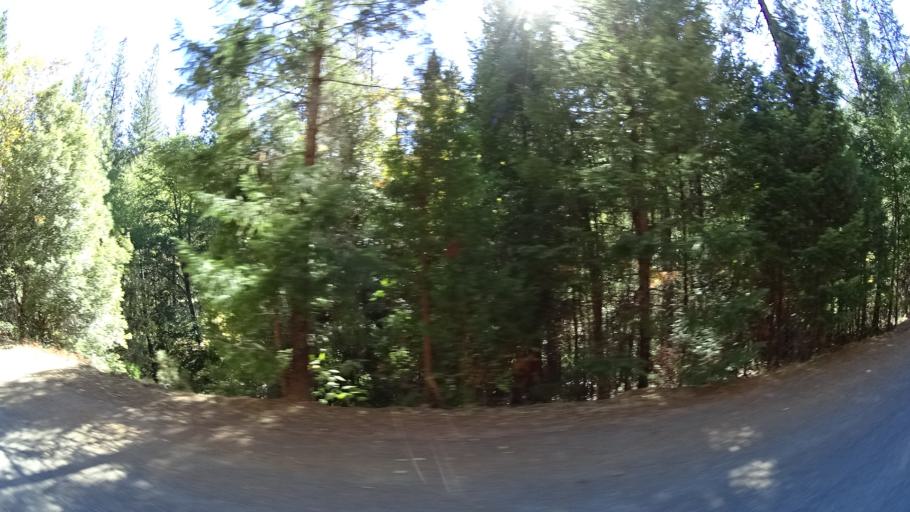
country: US
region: California
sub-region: Siskiyou County
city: Happy Camp
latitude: 41.3269
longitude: -123.0562
